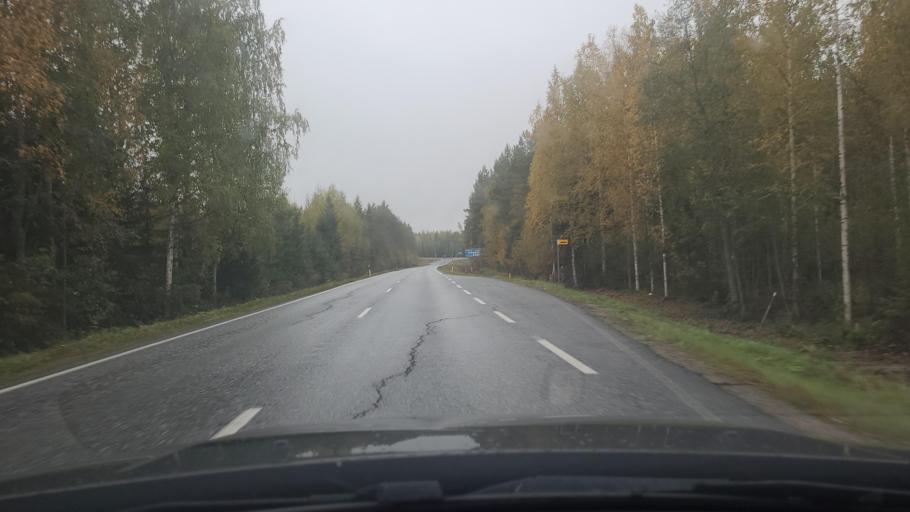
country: FI
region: Northern Savo
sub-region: Varkaus
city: Kangaslampi
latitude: 62.4593
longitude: 28.3245
